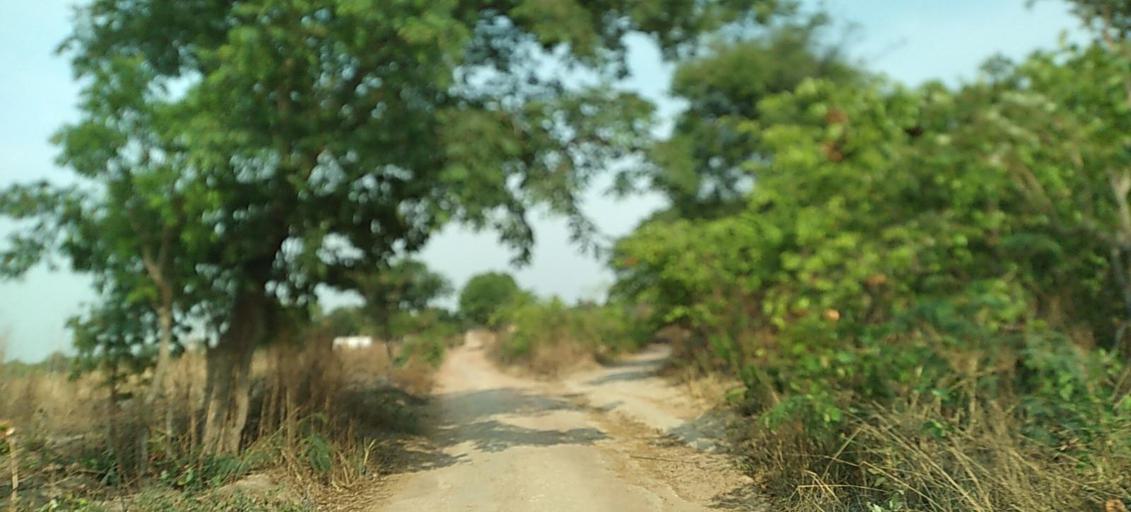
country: ZM
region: Copperbelt
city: Ndola
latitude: -13.2227
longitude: 28.6723
